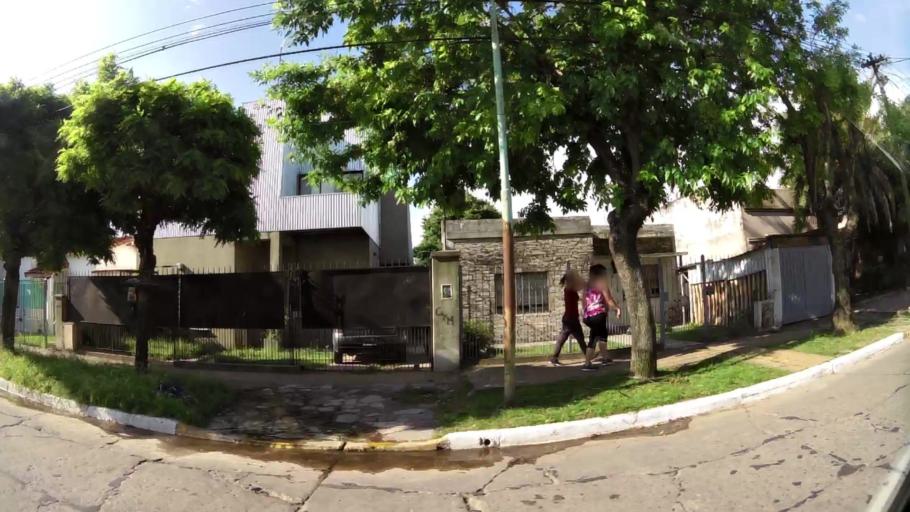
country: AR
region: Buenos Aires
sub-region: Partido de Merlo
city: Merlo
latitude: -34.6595
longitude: -58.7170
